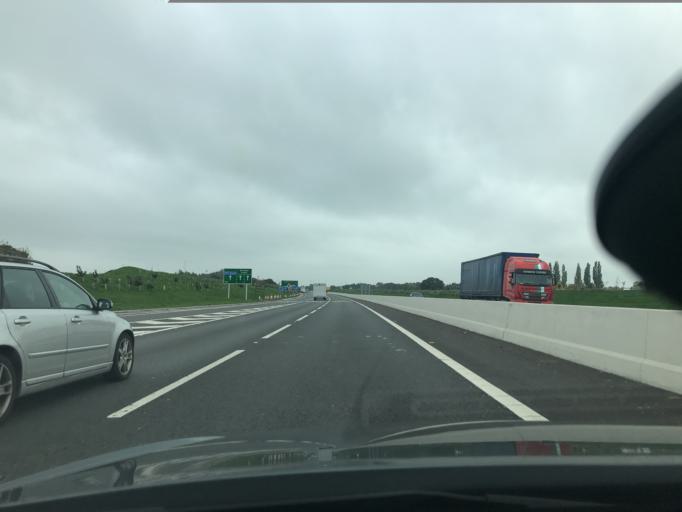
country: GB
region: England
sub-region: Cheshire East
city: Mere
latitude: 53.3187
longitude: -2.4204
